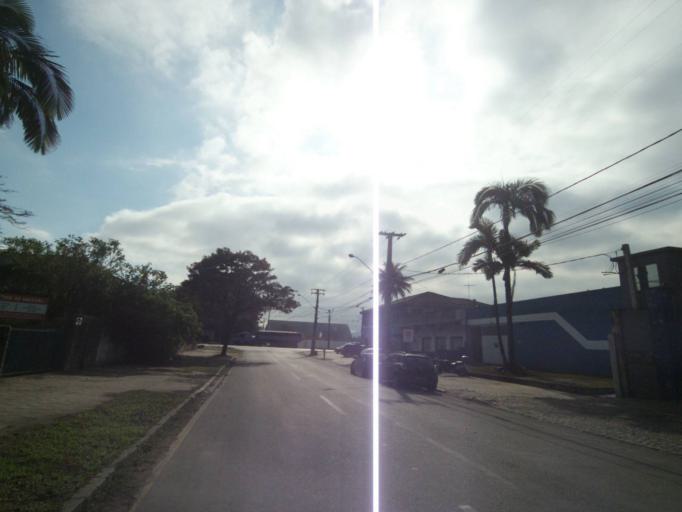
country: BR
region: Parana
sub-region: Paranagua
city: Paranagua
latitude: -25.5118
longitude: -48.5193
